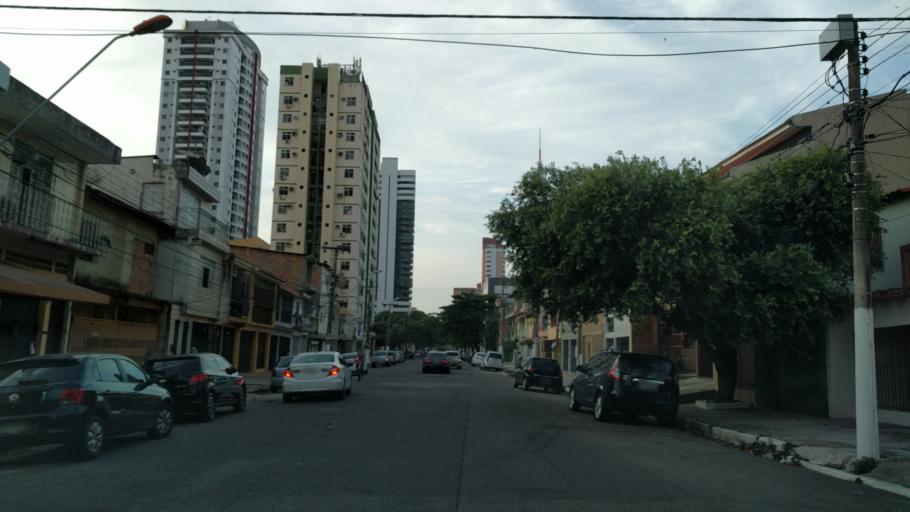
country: BR
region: Para
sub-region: Belem
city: Belem
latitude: -1.4659
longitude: -48.4884
